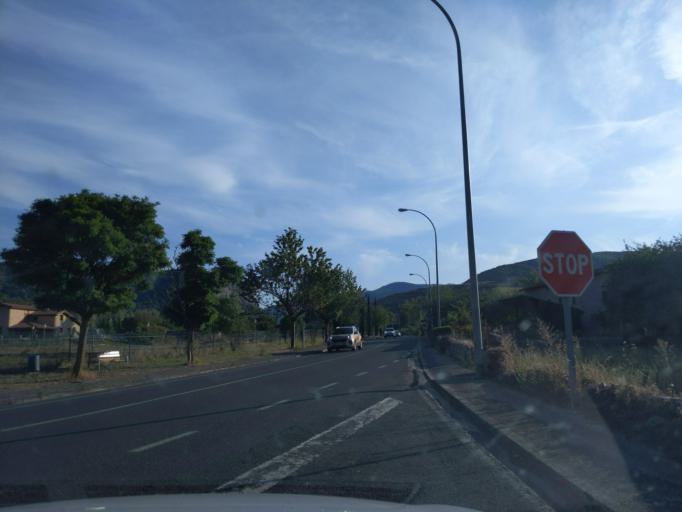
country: ES
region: La Rioja
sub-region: Provincia de La Rioja
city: Ojacastro
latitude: 42.3510
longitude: -2.9988
